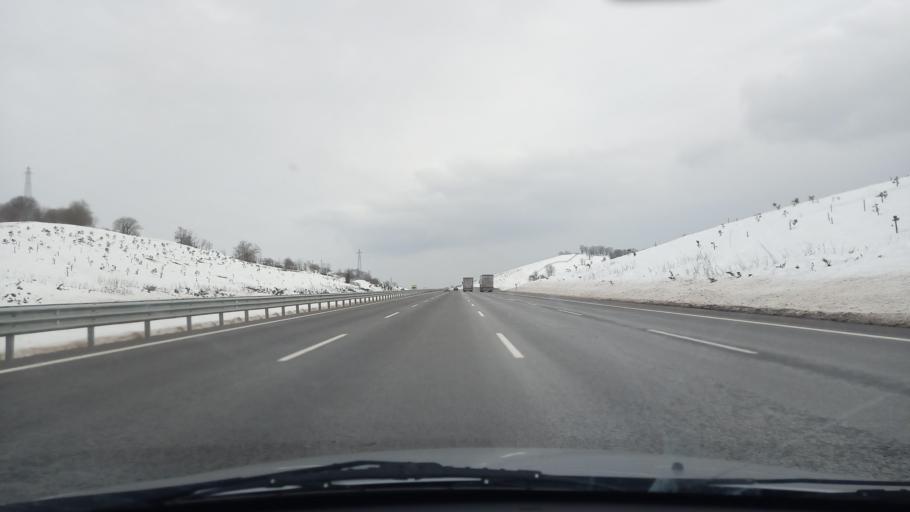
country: TR
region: Kocaeli
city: Korfez
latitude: 40.8643
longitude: 29.8156
